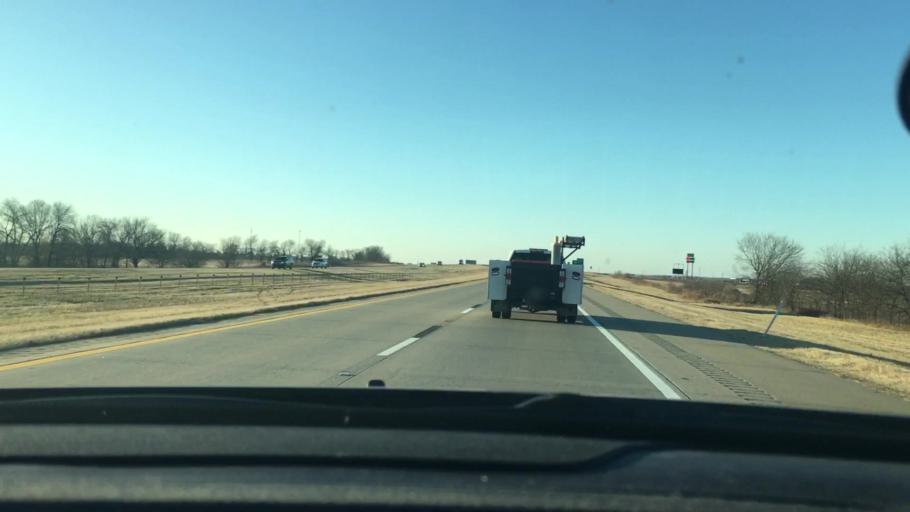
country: US
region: Oklahoma
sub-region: Carter County
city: Ardmore
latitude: 34.3395
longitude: -97.1498
